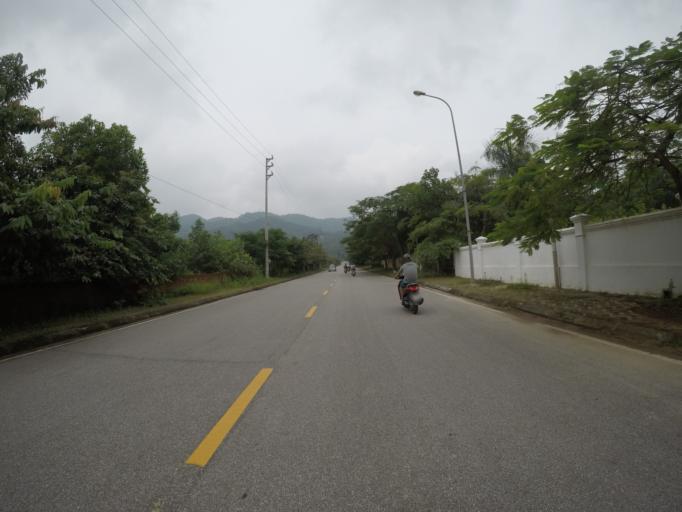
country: VN
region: Ha Noi
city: Soc Son
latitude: 21.2848
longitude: 105.8376
